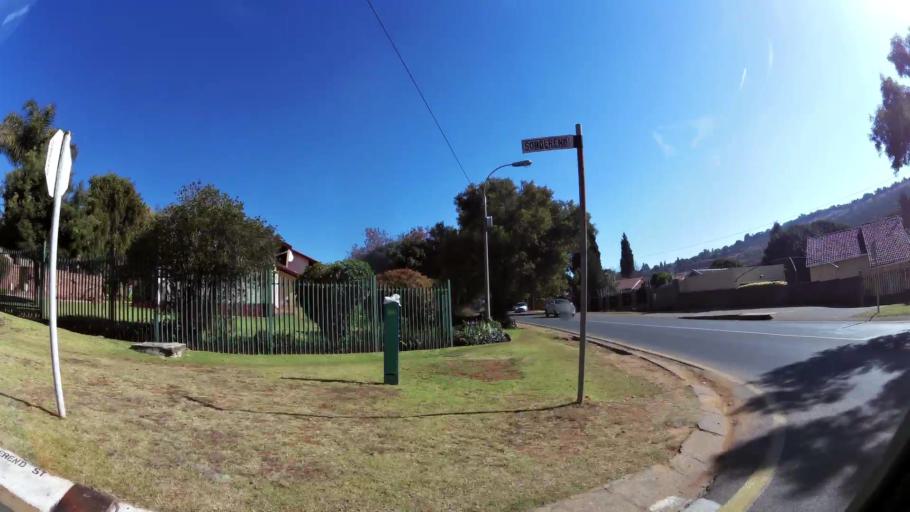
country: ZA
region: Gauteng
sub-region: City of Johannesburg Metropolitan Municipality
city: Roodepoort
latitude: -26.1167
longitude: 27.8696
